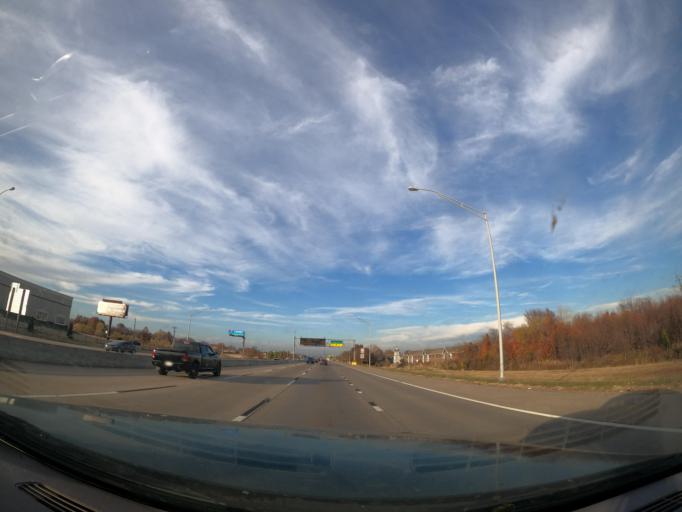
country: US
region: Oklahoma
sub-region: Tulsa County
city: Broken Arrow
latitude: 36.0675
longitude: -95.8593
